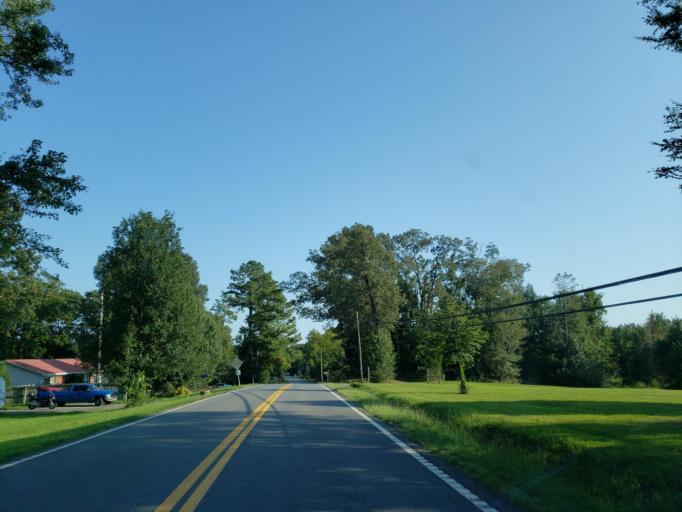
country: US
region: Tennessee
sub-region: Bradley County
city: Wildwood Lake
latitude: 35.0398
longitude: -84.8043
